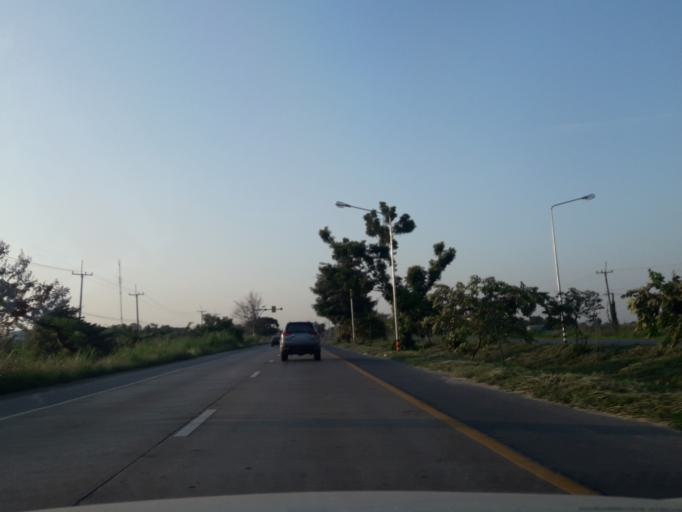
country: TH
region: Phra Nakhon Si Ayutthaya
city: Phra Nakhon Si Ayutthaya
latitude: 14.3243
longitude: 100.5278
